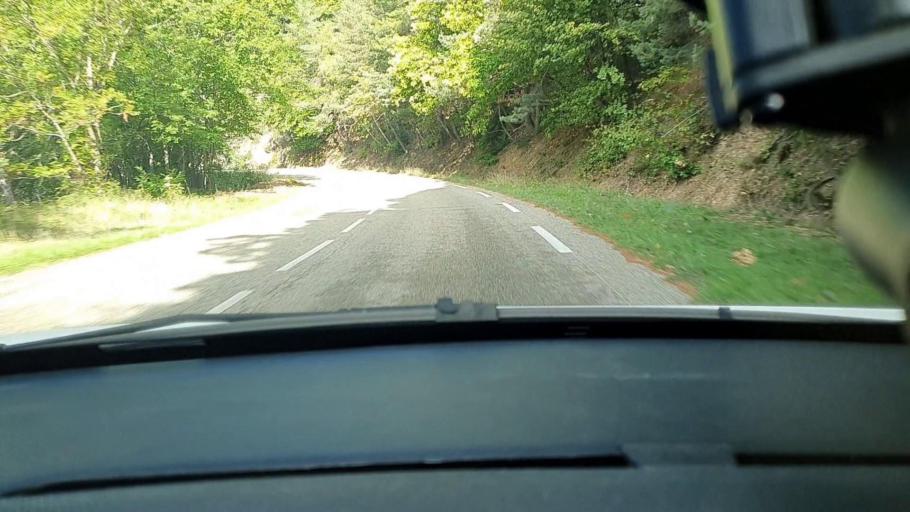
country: FR
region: Rhone-Alpes
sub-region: Departement de l'Ardeche
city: Les Vans
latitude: 44.4223
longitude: 3.9795
